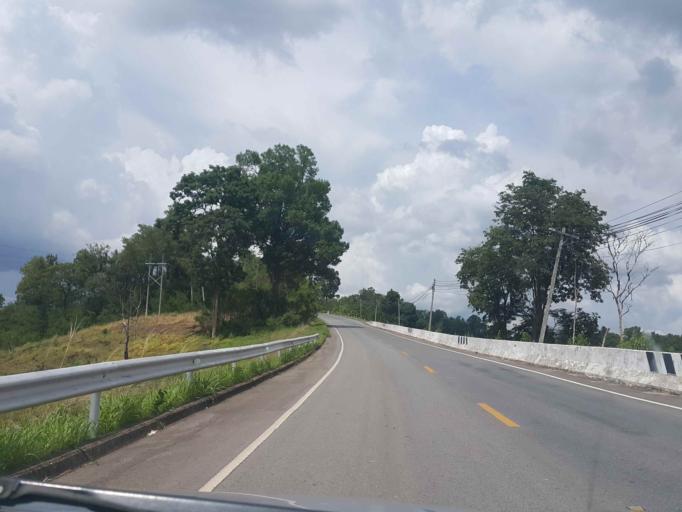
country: TH
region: Nan
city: Ban Luang
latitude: 18.8732
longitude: 100.5642
